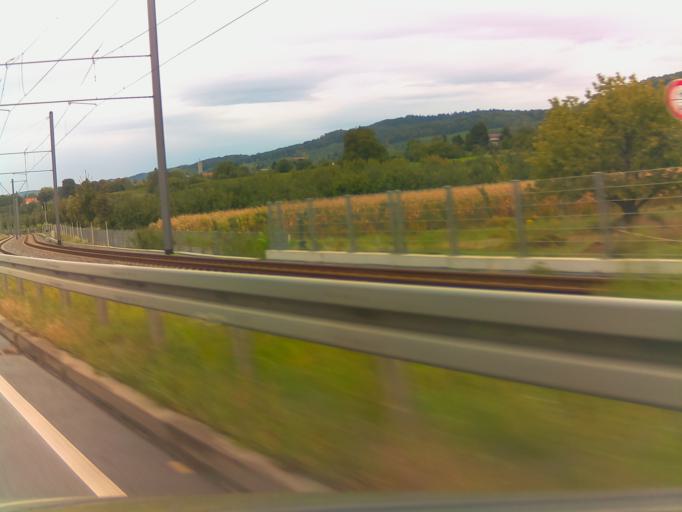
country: DE
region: Baden-Wuerttemberg
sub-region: Karlsruhe Region
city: Schriesheim
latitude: 49.5008
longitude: 8.6563
